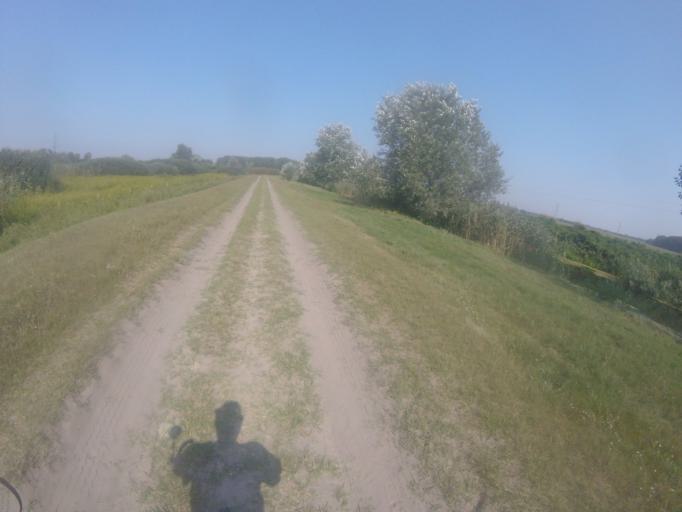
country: HU
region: Bacs-Kiskun
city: Baja
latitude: 46.2143
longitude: 18.9566
